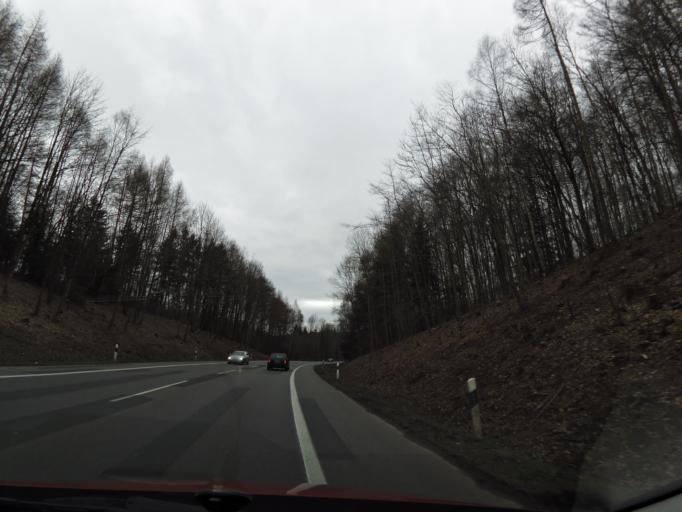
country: DE
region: Lower Saxony
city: Wollershausen
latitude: 51.6230
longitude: 10.2654
